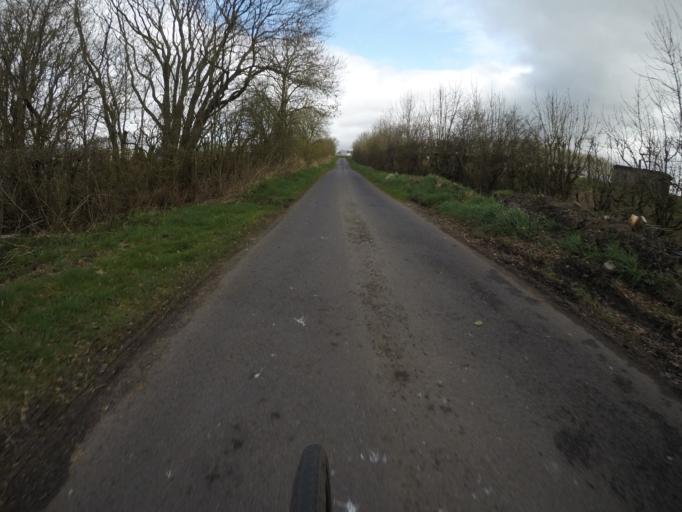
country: GB
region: Scotland
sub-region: North Ayrshire
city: Springside
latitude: 55.6591
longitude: -4.6095
